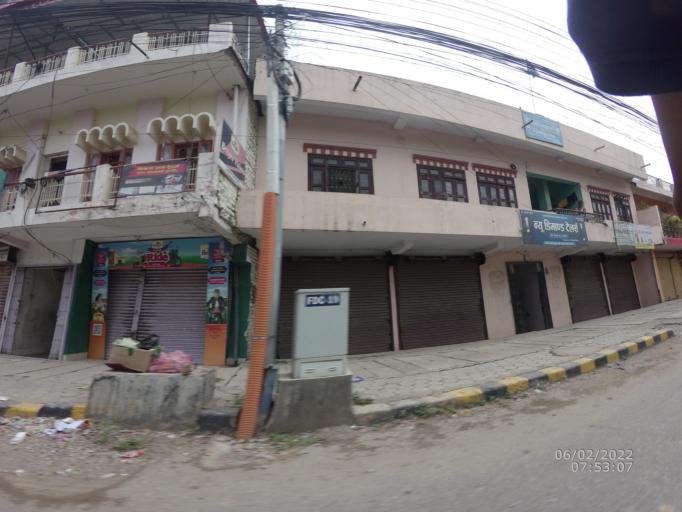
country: NP
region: Western Region
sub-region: Lumbini Zone
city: Bhairahawa
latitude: 27.5085
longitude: 83.4557
